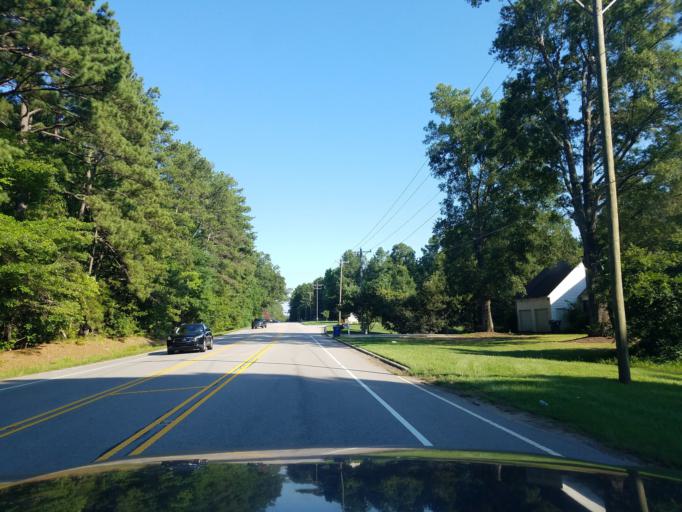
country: US
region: North Carolina
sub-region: Wake County
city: Green Level
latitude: 35.8772
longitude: -78.9516
